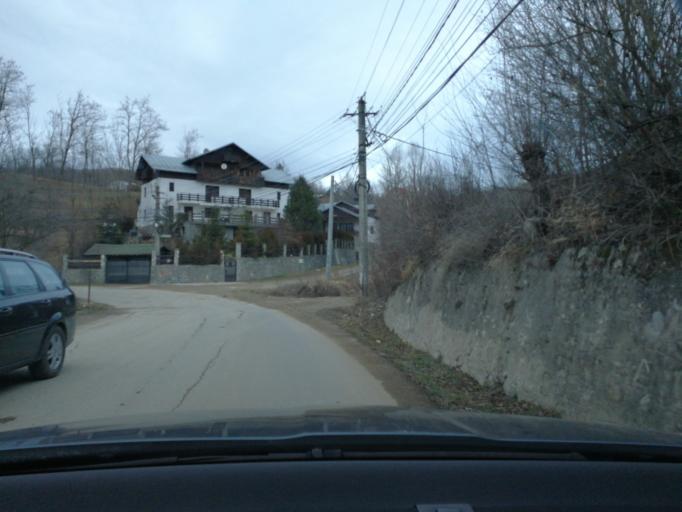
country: RO
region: Prahova
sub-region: Oras Breaza
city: Valea Tarsei
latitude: 45.1812
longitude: 25.6420
